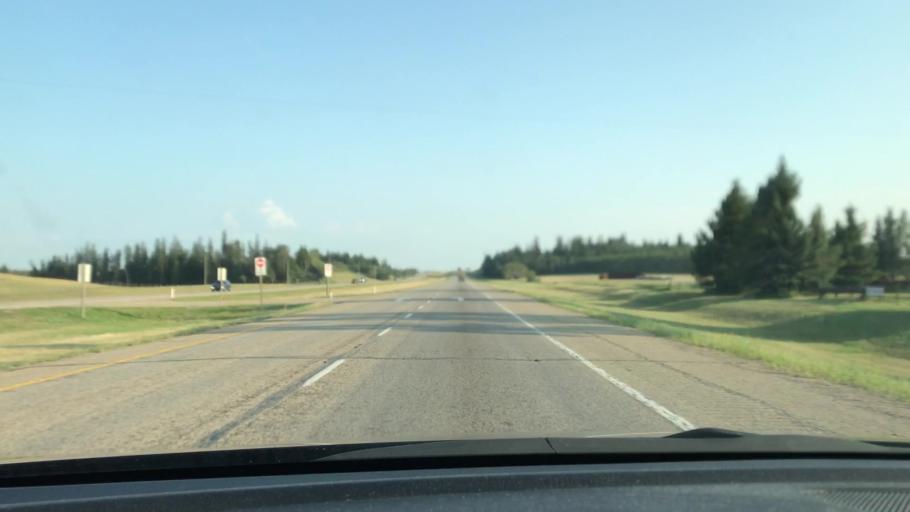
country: CA
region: Alberta
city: Ponoka
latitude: 52.6006
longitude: -113.6635
